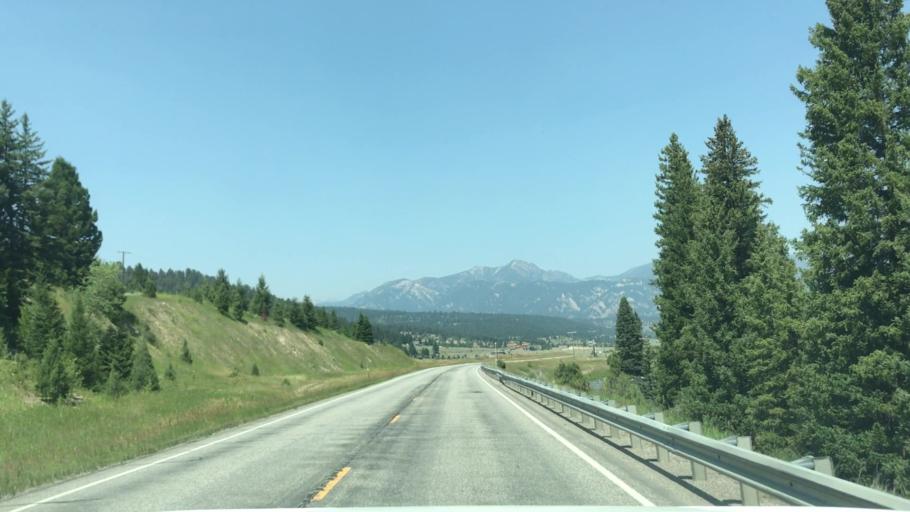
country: US
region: Montana
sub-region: Gallatin County
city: Big Sky
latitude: 45.2106
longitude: -111.2464
